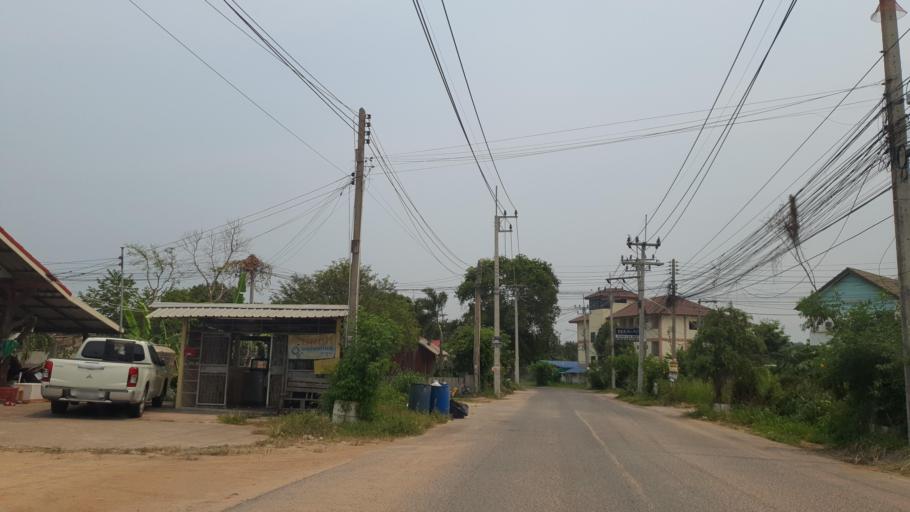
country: TH
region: Chon Buri
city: Phatthaya
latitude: 12.8974
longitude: 100.9068
